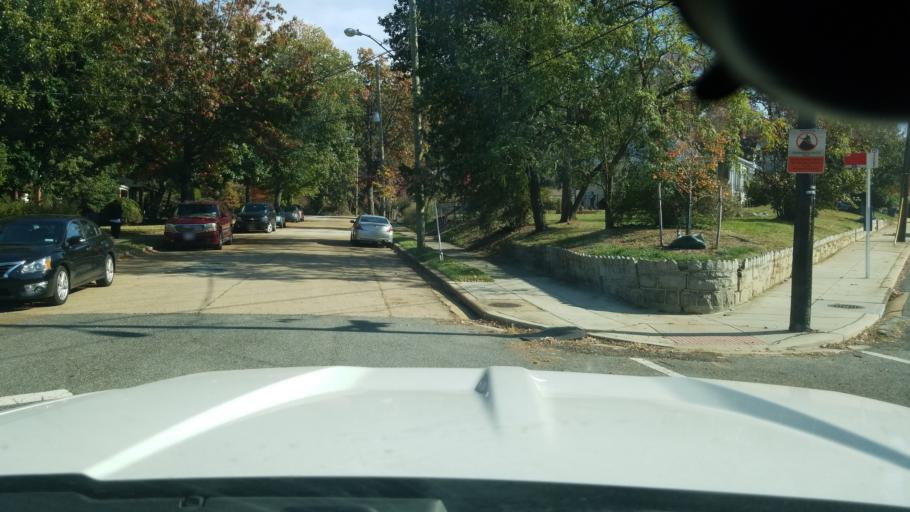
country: US
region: Maryland
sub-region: Prince George's County
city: Mount Rainier
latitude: 38.9396
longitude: -76.9737
